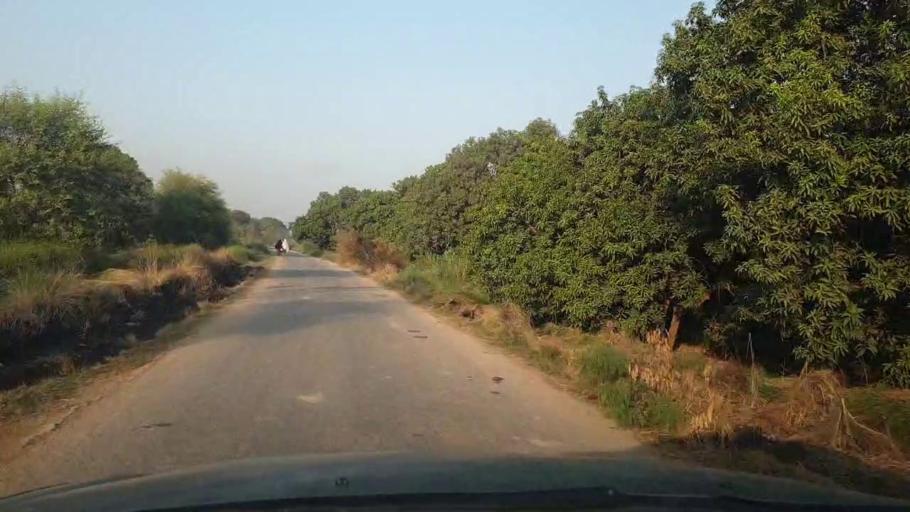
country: PK
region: Sindh
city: Tando Jam
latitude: 25.4180
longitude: 68.4899
